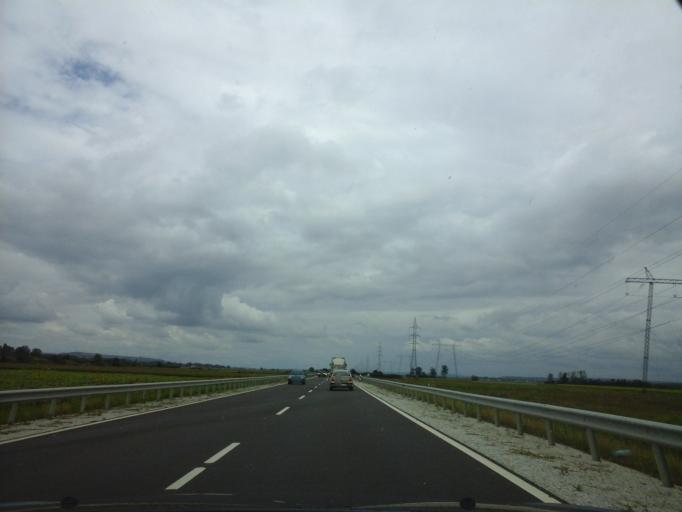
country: HU
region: Borsod-Abauj-Zemplen
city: Arnot
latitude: 48.1276
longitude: 20.8393
